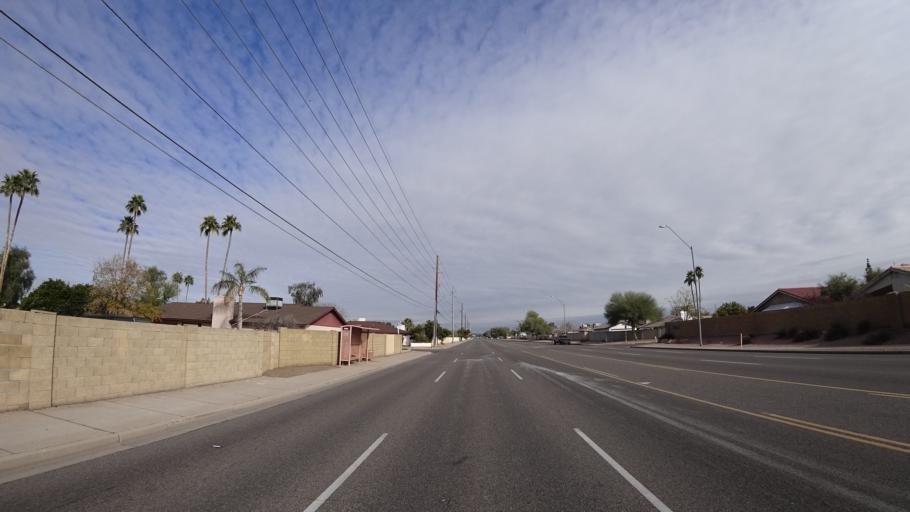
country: US
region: Arizona
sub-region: Maricopa County
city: Glendale
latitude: 33.5995
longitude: -112.1514
